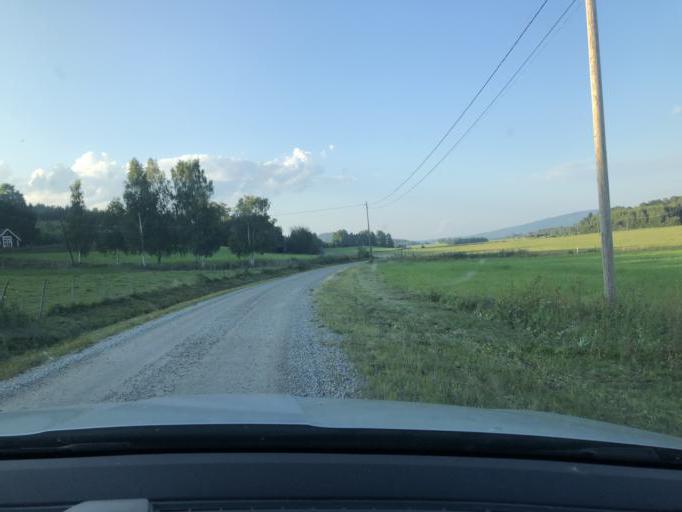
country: SE
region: Vaesternorrland
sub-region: Kramfors Kommun
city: Bollstabruk
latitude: 63.0592
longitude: 17.7328
